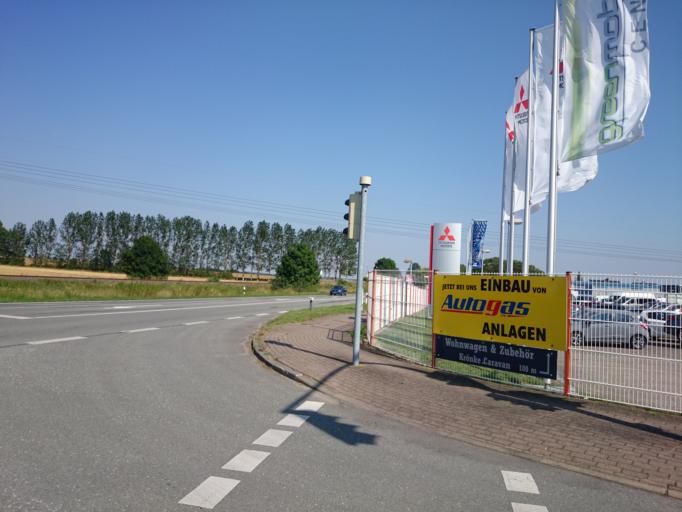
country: DE
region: Mecklenburg-Vorpommern
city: Tessin
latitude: 54.0347
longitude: 12.4395
